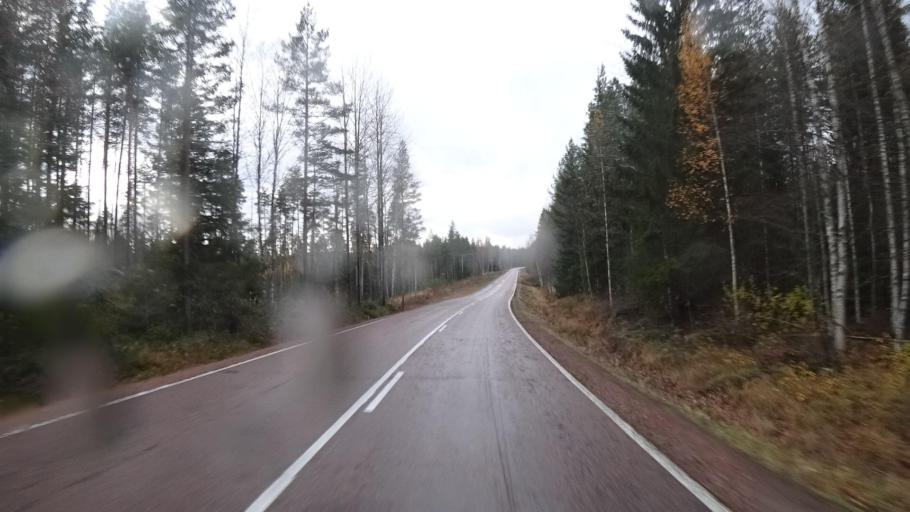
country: FI
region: Southern Savonia
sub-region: Mikkeli
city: Kangasniemi
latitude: 62.0759
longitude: 26.6907
